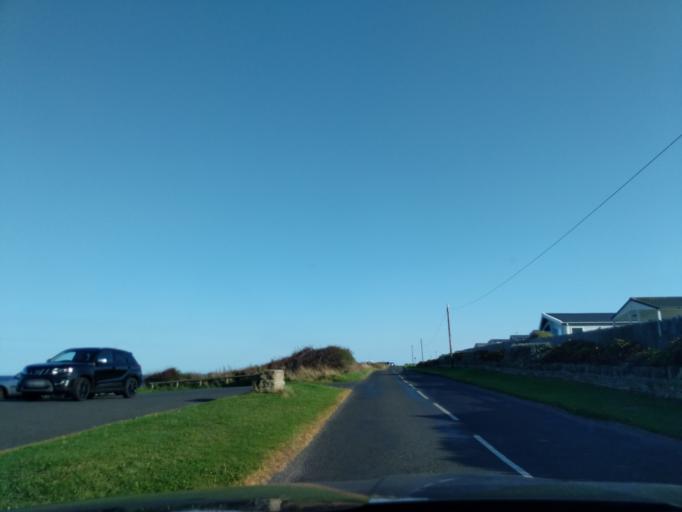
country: GB
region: England
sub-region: Northumberland
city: Lynemouth
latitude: 55.2305
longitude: -1.5319
